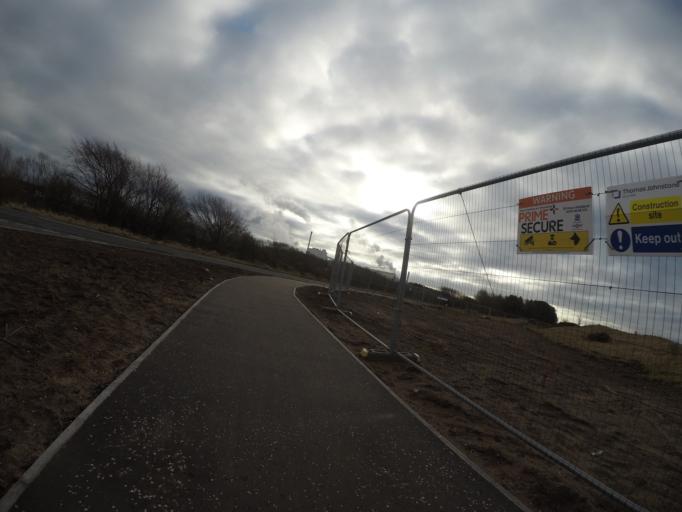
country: GB
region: Scotland
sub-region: North Ayrshire
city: Irvine
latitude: 55.5873
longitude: -4.6487
